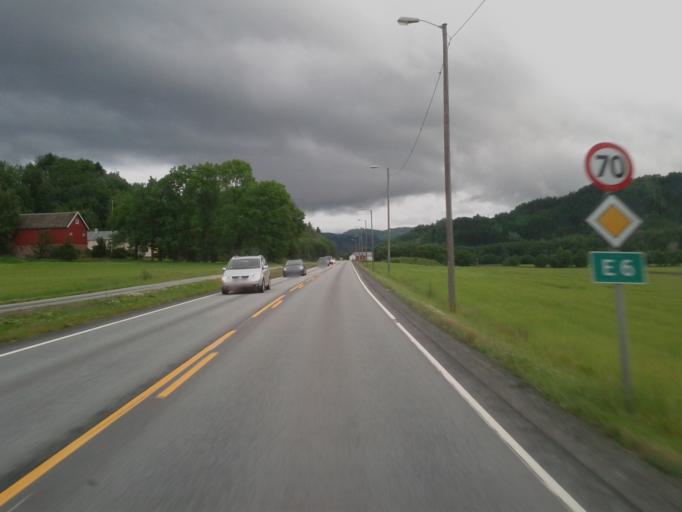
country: NO
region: Sor-Trondelag
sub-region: Melhus
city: Lundamo
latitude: 63.1353
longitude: 10.2521
